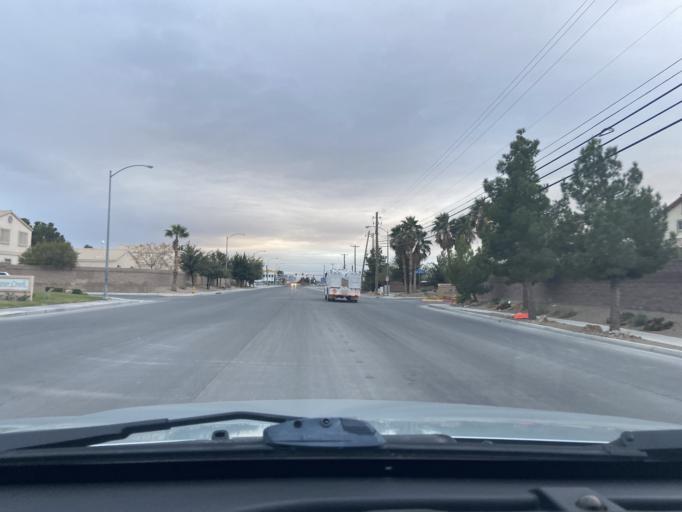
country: US
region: Nevada
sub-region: Clark County
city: Las Vegas
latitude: 36.2202
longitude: -115.1886
